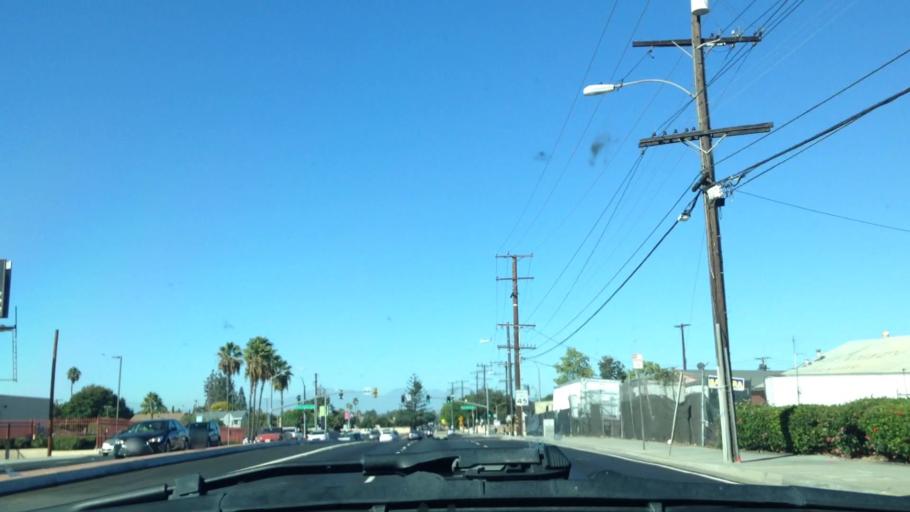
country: US
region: California
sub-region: Orange County
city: Santa Ana
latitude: 33.7503
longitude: -117.9038
